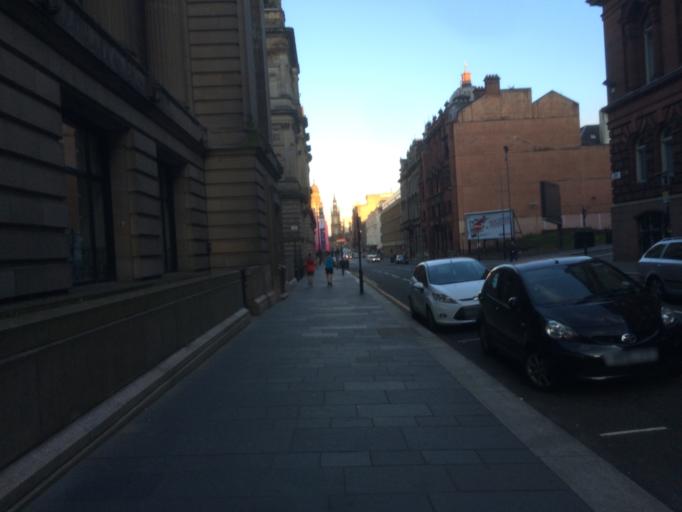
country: GB
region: Scotland
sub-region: Glasgow City
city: Glasgow
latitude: 55.8612
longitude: -4.2466
